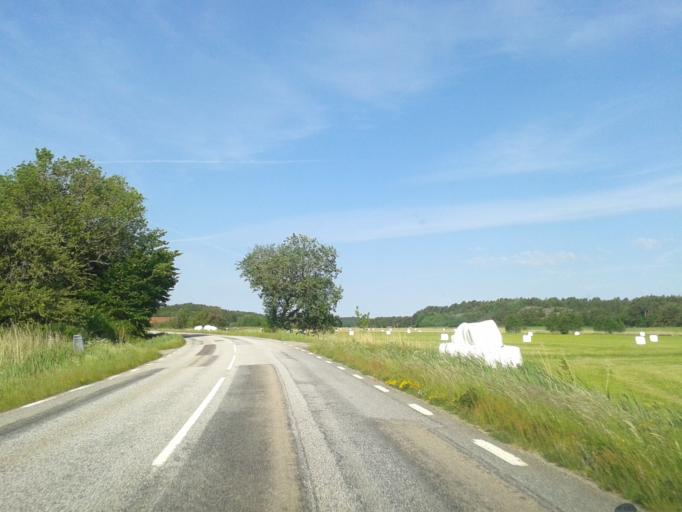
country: SE
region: Vaestra Goetaland
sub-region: Stromstads Kommun
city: Stroemstad
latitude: 58.8616
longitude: 11.2470
